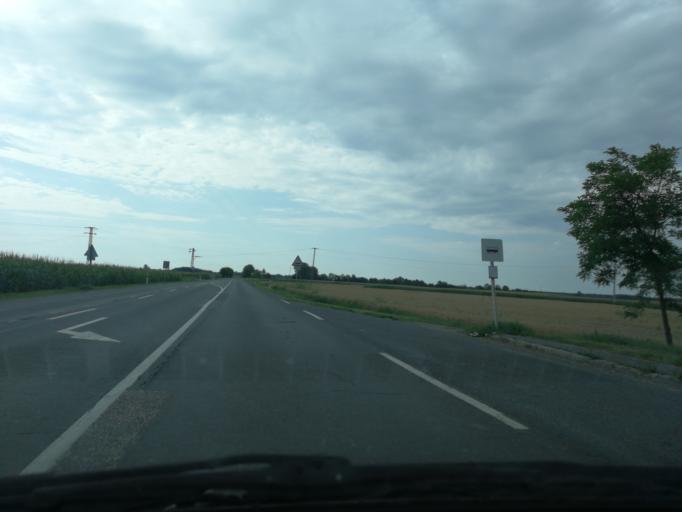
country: HU
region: Bacs-Kiskun
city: Dusnok
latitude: 46.4197
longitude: 18.9427
